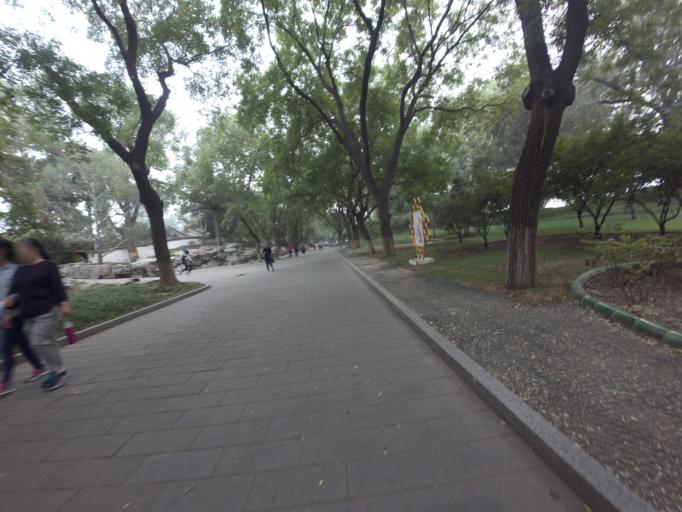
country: CN
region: Beijing
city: Jingshan
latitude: 39.9294
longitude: 116.3857
